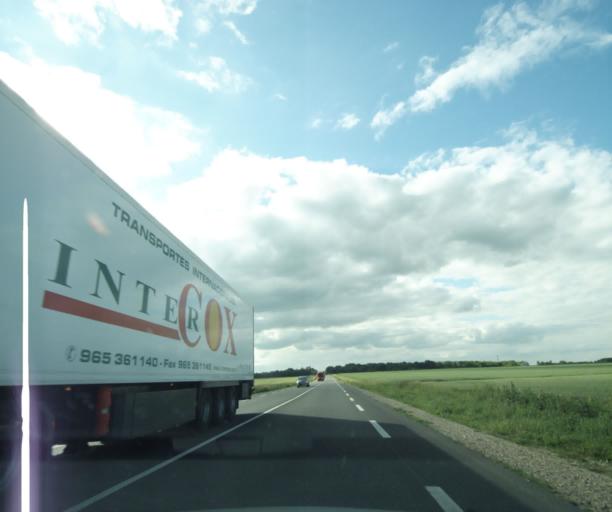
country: FR
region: Centre
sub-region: Departement d'Eure-et-Loir
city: Sours
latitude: 48.3832
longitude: 1.5822
